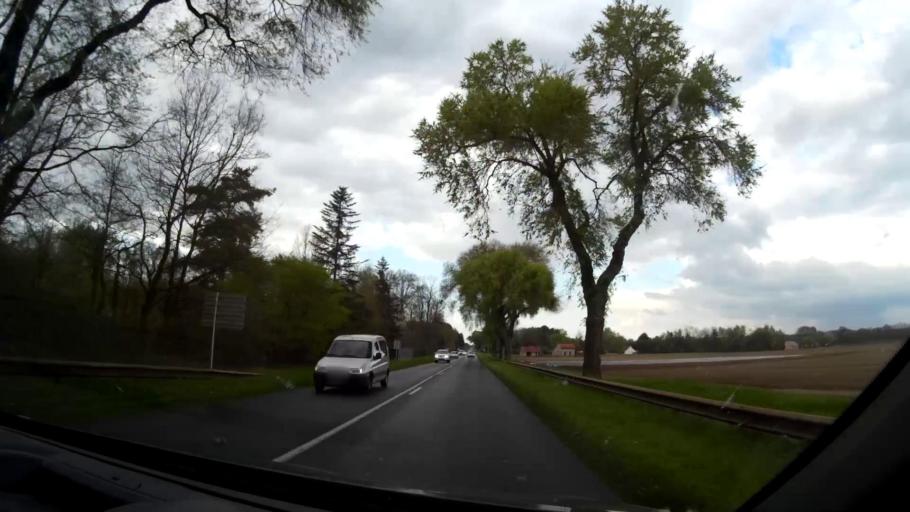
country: FR
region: Centre
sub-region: Departement du Loir-et-Cher
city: Contres
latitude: 47.4403
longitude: 1.4270
